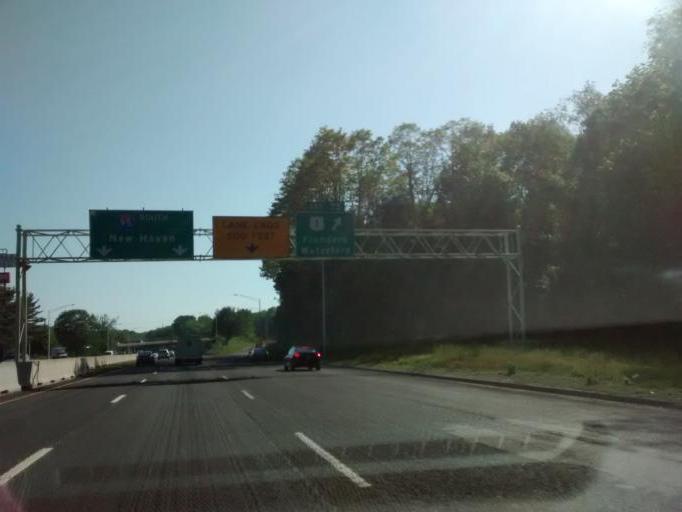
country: US
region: Connecticut
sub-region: New London County
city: Niantic
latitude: 41.3723
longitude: -72.1988
